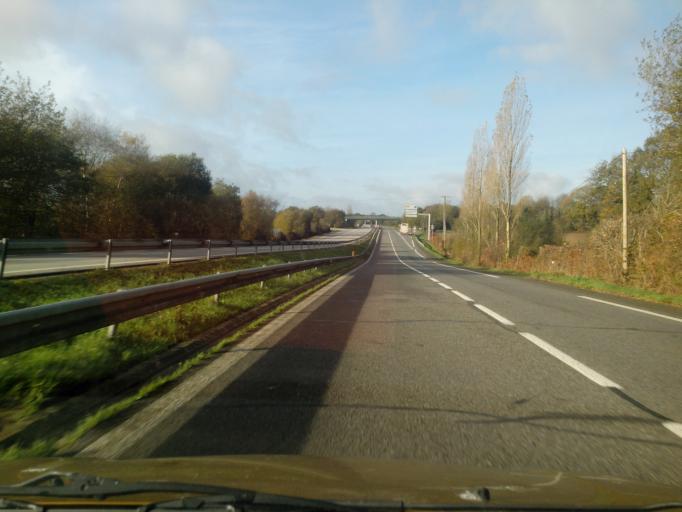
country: FR
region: Brittany
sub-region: Departement du Morbihan
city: Reguiny
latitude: 47.9205
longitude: -2.7155
